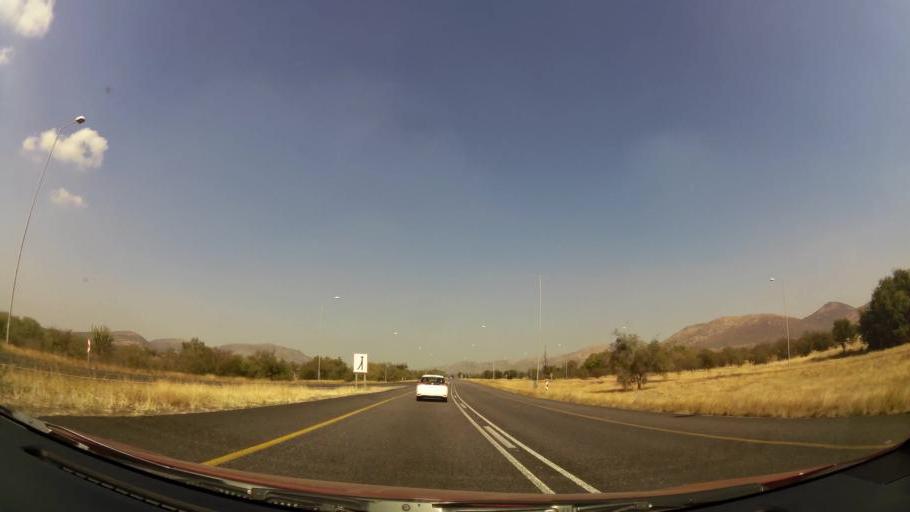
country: ZA
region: North-West
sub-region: Bojanala Platinum District Municipality
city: Rustenburg
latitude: -25.6157
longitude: 27.1542
